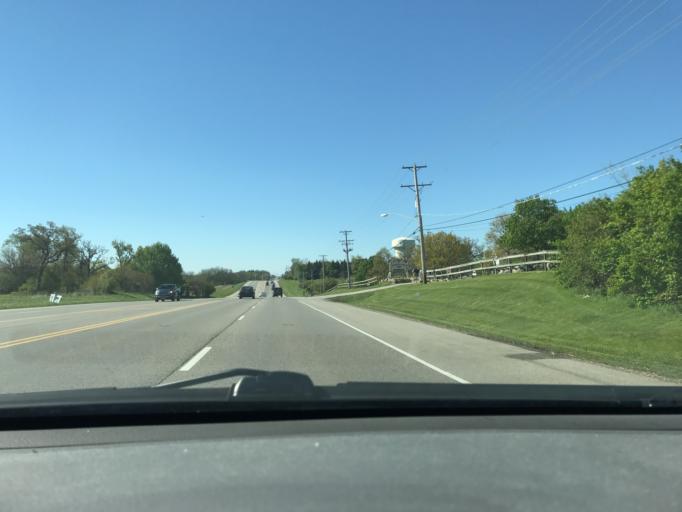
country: US
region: Illinois
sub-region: Kane County
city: Sleepy Hollow
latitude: 42.1164
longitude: -88.3352
